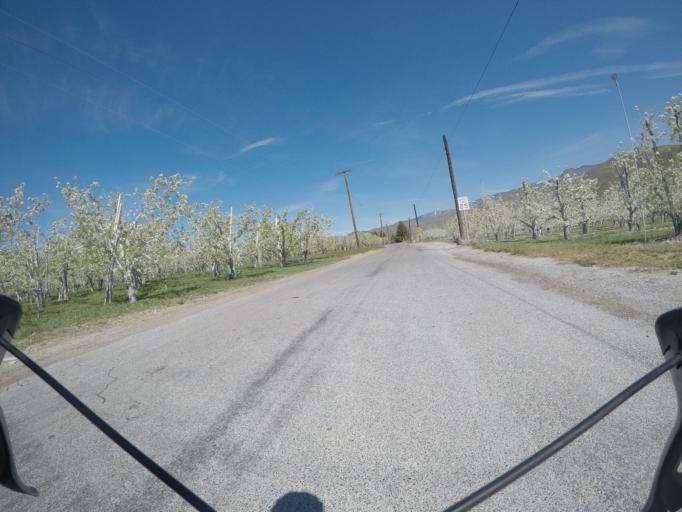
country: US
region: Washington
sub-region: Chelan County
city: Cashmere
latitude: 47.4911
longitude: -120.4315
